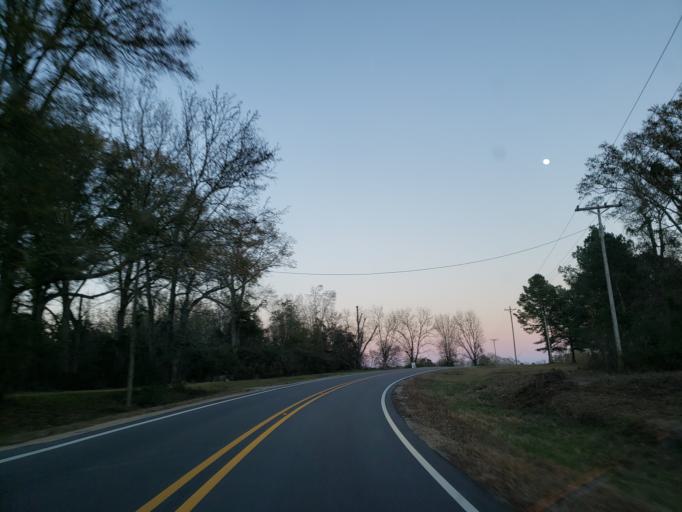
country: US
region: Mississippi
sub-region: Jones County
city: Ellisville
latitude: 31.5793
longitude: -89.2831
